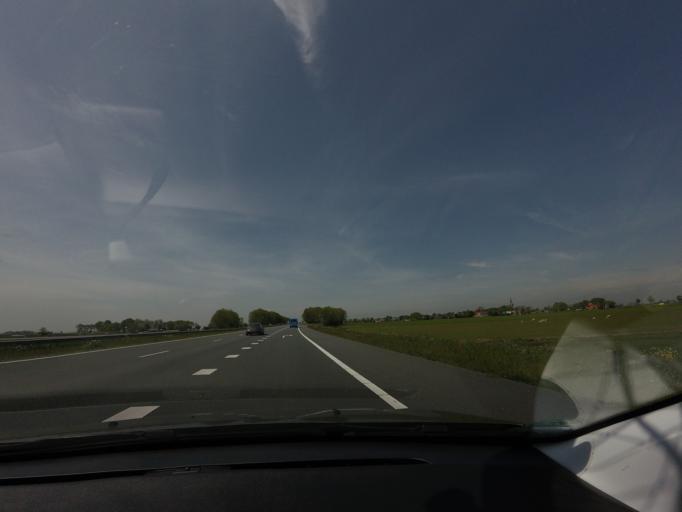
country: NL
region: Friesland
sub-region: Sudwest Fryslan
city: IJlst
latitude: 53.0451
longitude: 5.5833
